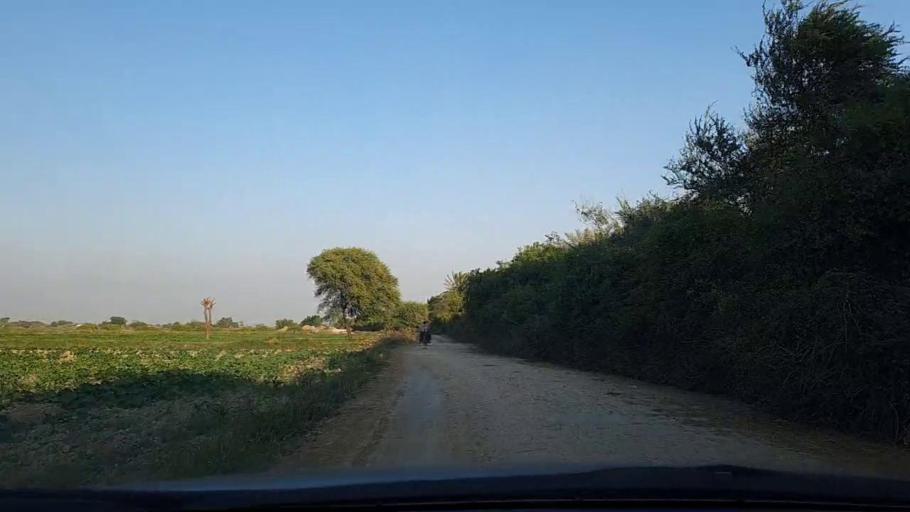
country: PK
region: Sindh
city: Mirpur Sakro
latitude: 24.5212
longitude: 67.6420
